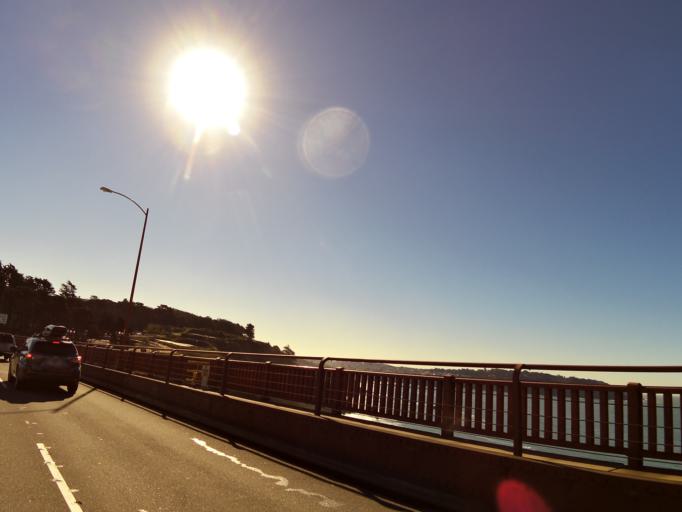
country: US
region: California
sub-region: Marin County
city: Sausalito
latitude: 37.8089
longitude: -122.4775
